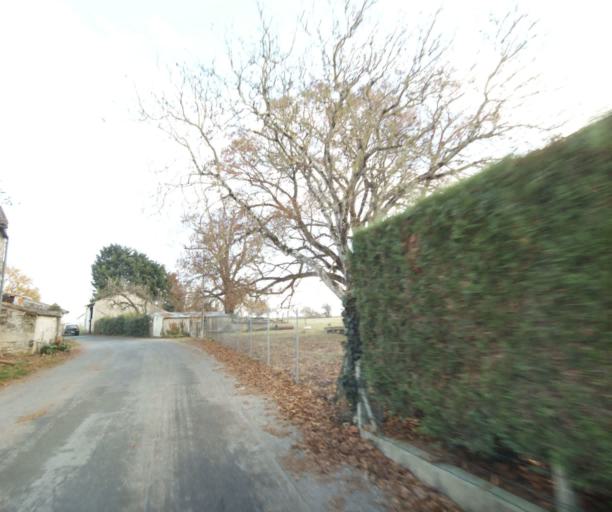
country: FR
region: Poitou-Charentes
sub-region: Departement de la Charente-Maritime
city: Les Gonds
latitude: 45.7102
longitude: -0.6121
